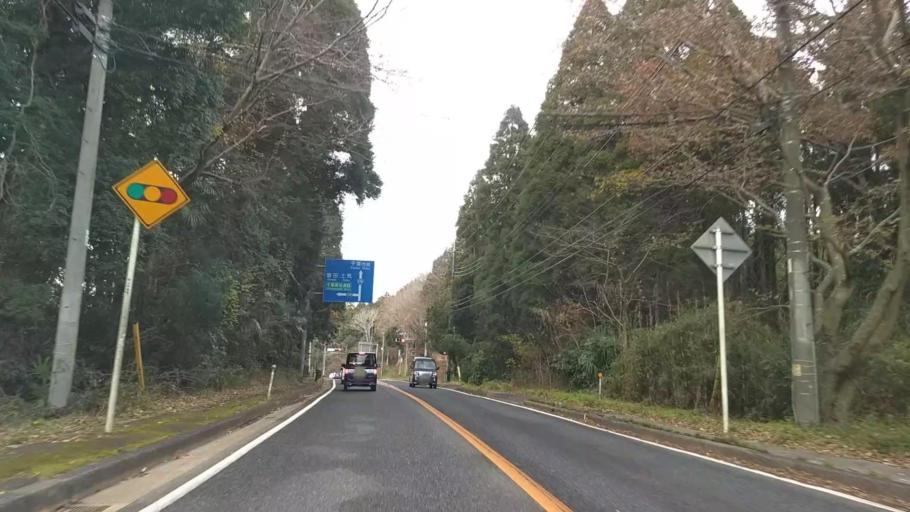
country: JP
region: Chiba
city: Oami
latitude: 35.5805
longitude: 140.2633
